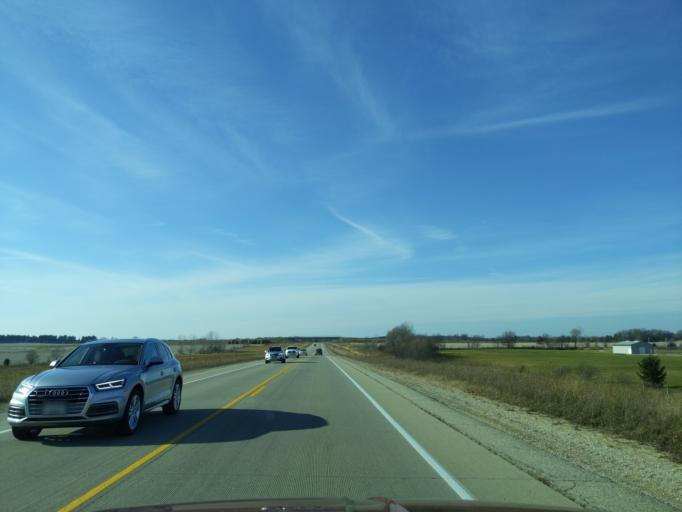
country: US
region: Wisconsin
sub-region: Walworth County
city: Whitewater
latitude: 42.8212
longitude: -88.7530
